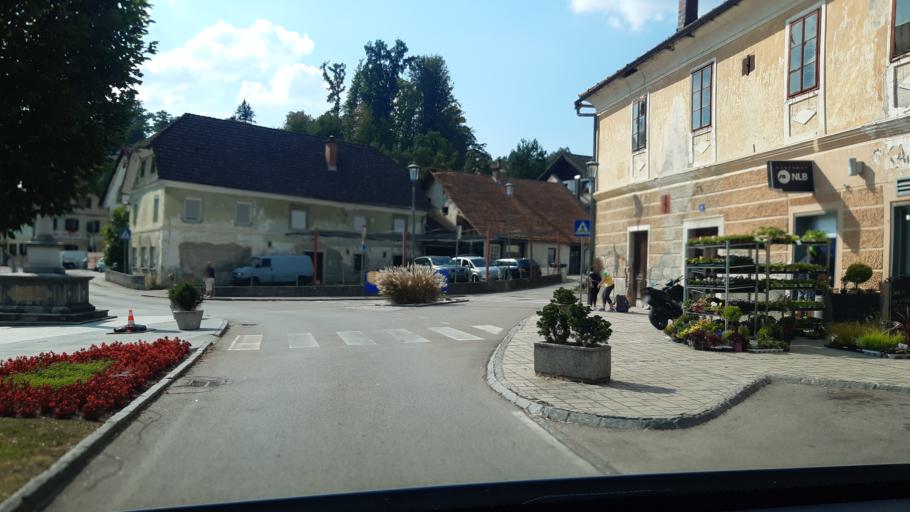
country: SI
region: Lukovica
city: Lukovica pri Domzalah
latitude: 46.1699
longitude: 14.6911
